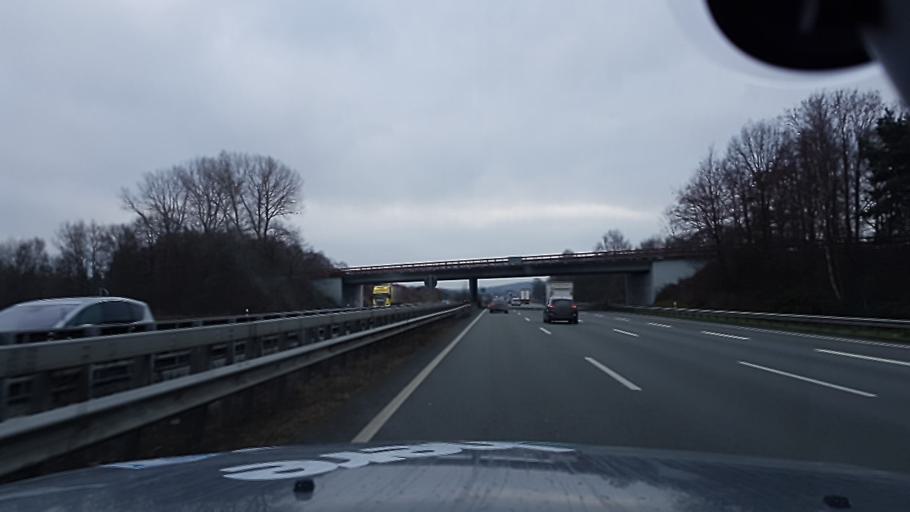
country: DE
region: Lower Saxony
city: Wallenhorst
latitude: 52.3957
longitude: 8.0377
